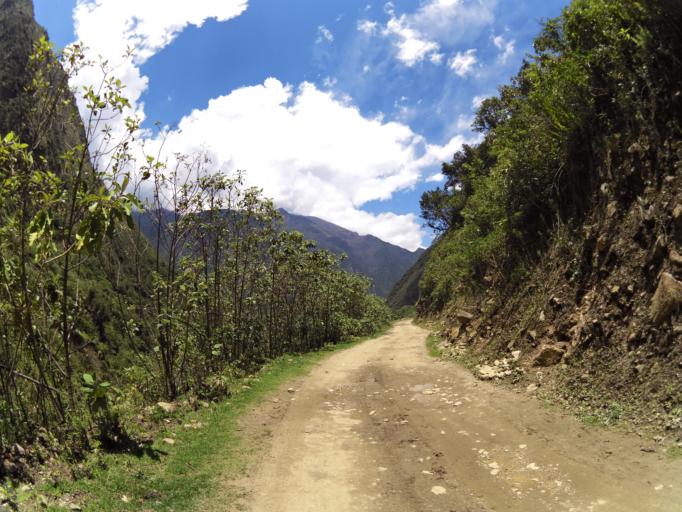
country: PE
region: Cusco
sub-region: Provincia de La Convencion
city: Santa Teresa
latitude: -13.3269
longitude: -72.6649
